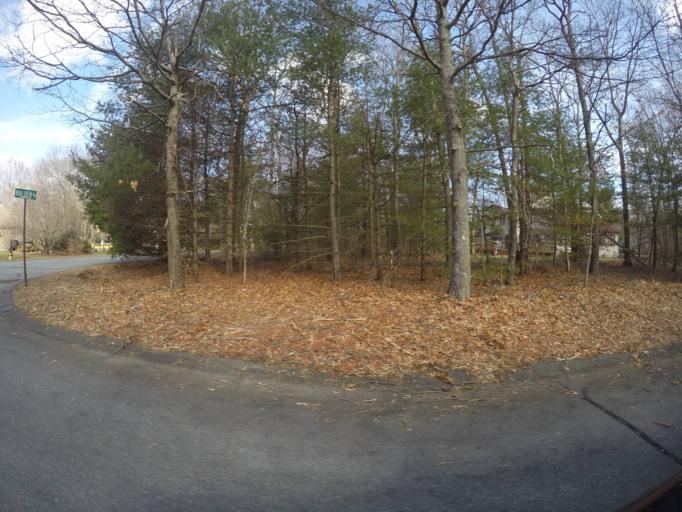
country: US
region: Massachusetts
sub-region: Bristol County
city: Easton
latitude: 42.0116
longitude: -71.1420
